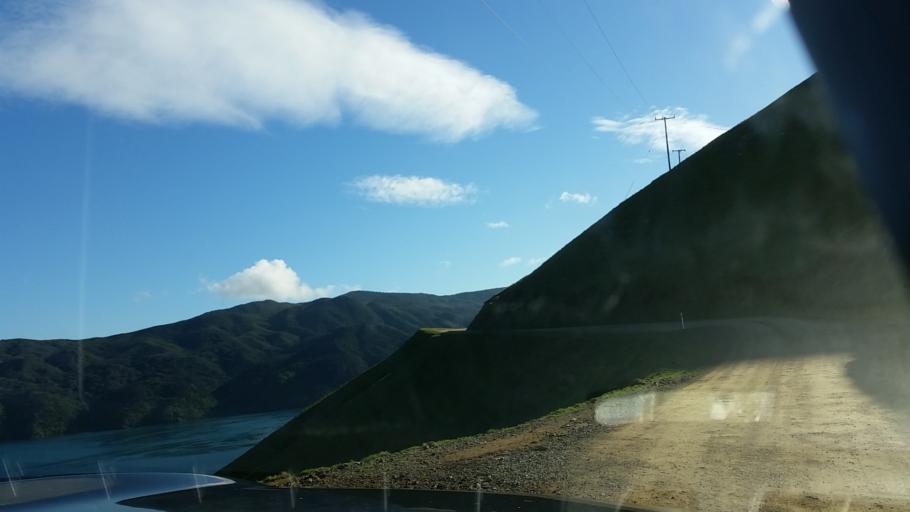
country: NZ
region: Marlborough
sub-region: Marlborough District
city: Picton
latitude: -40.9350
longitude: 173.8416
